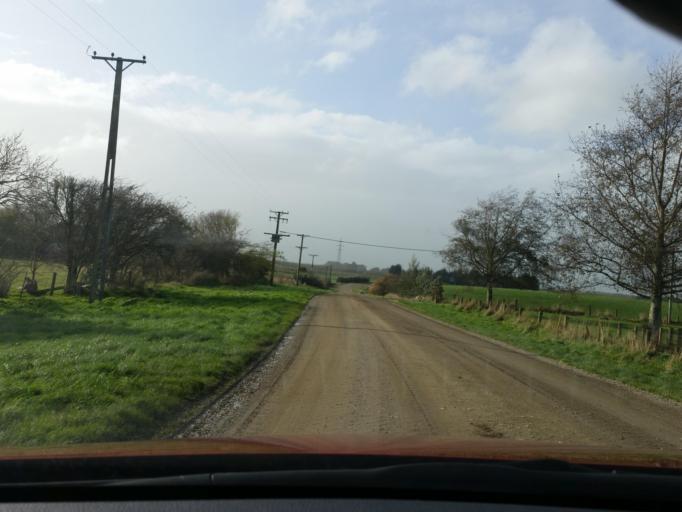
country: NZ
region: Southland
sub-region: Invercargill City
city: Invercargill
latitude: -46.3090
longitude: 168.3781
